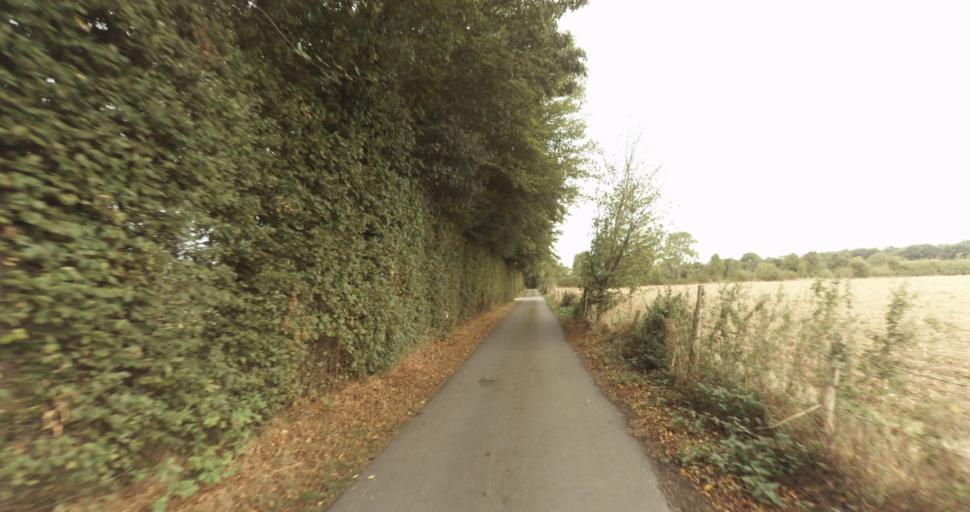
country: FR
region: Lower Normandy
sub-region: Departement de l'Orne
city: Gace
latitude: 48.8682
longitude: 0.3111
